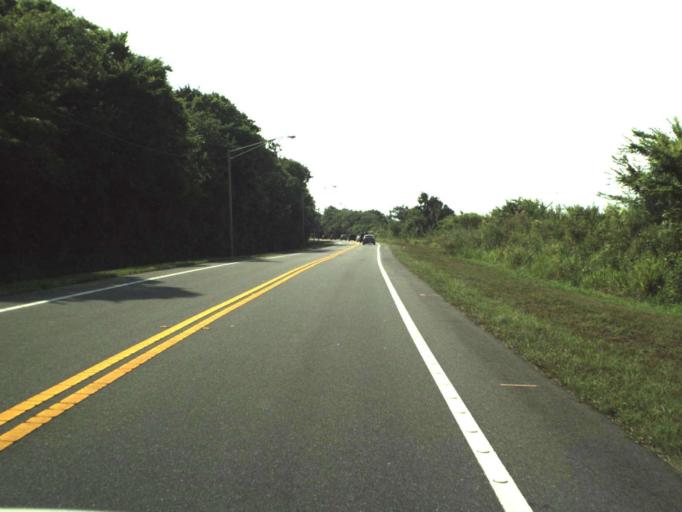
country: US
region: Florida
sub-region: Seminole County
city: Sanford
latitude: 28.8270
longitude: -81.3080
